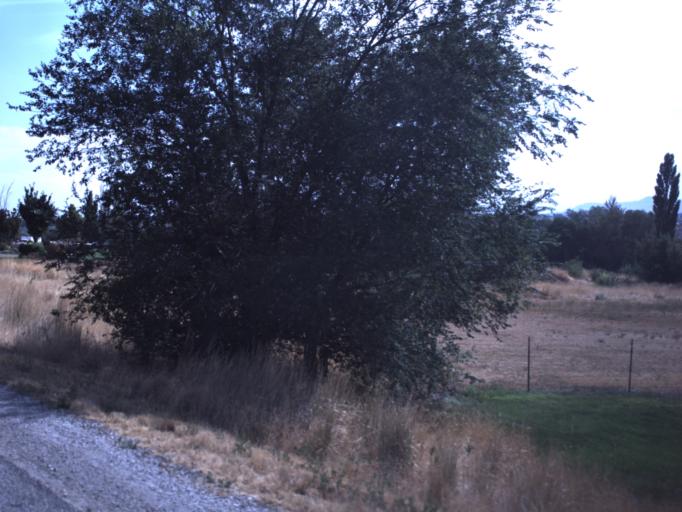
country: US
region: Utah
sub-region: Box Elder County
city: Elwood
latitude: 41.7196
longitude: -112.0933
